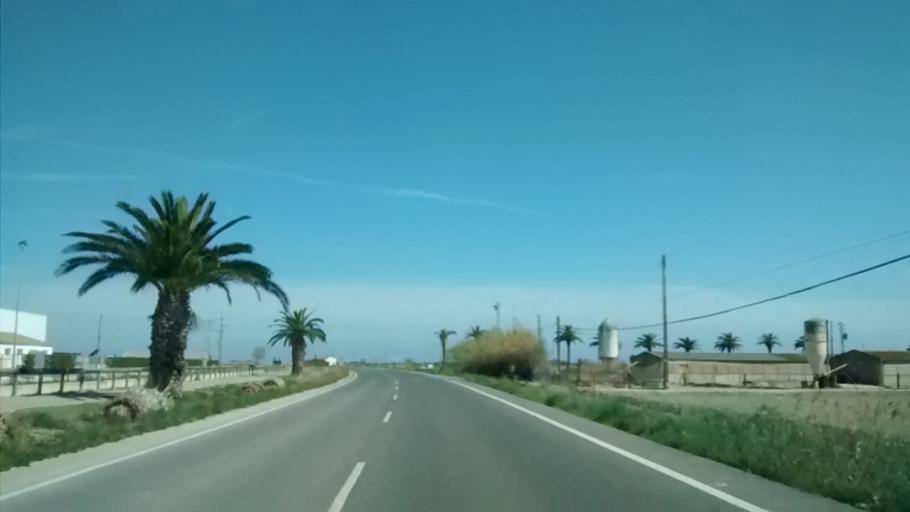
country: ES
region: Catalonia
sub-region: Provincia de Tarragona
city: Deltebre
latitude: 40.7074
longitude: 0.7636
